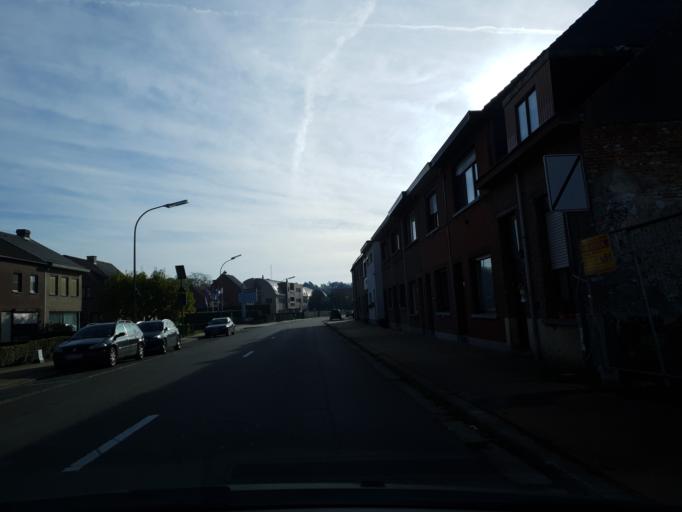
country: BE
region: Flanders
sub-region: Provincie Oost-Vlaanderen
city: Sint-Niklaas
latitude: 51.1559
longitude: 4.1650
